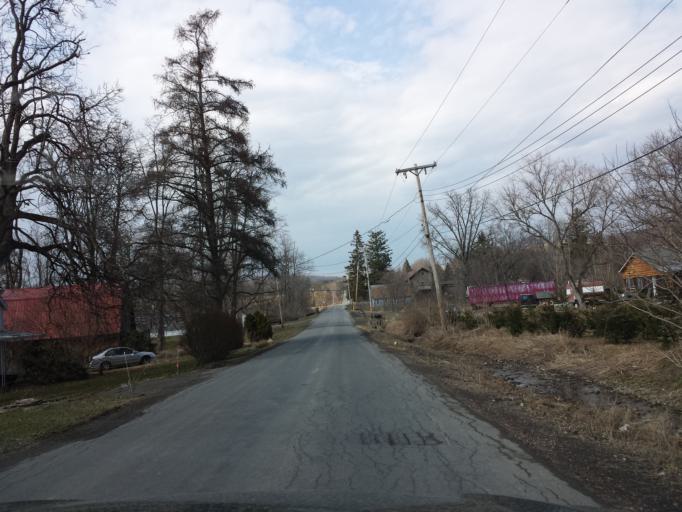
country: US
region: New York
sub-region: Tompkins County
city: Dryden
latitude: 42.3915
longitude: -76.3504
